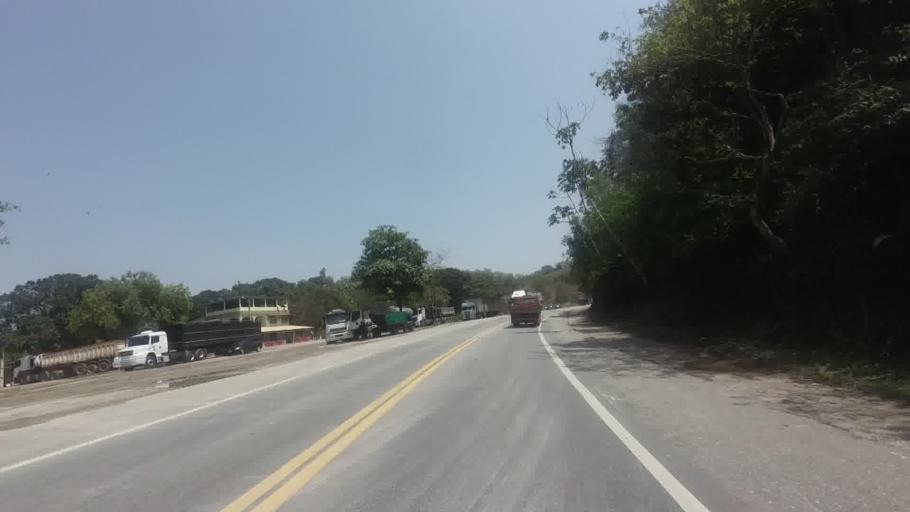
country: BR
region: Espirito Santo
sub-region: Rio Novo Do Sul
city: Rio Novo do Sul
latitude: -20.8900
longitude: -40.9923
